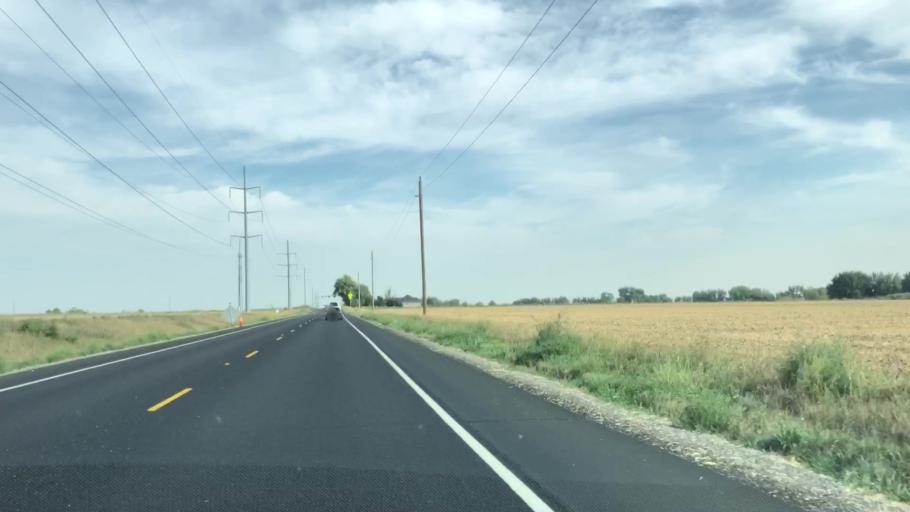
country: US
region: Colorado
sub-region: Larimer County
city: Loveland
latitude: 40.4546
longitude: -105.0442
